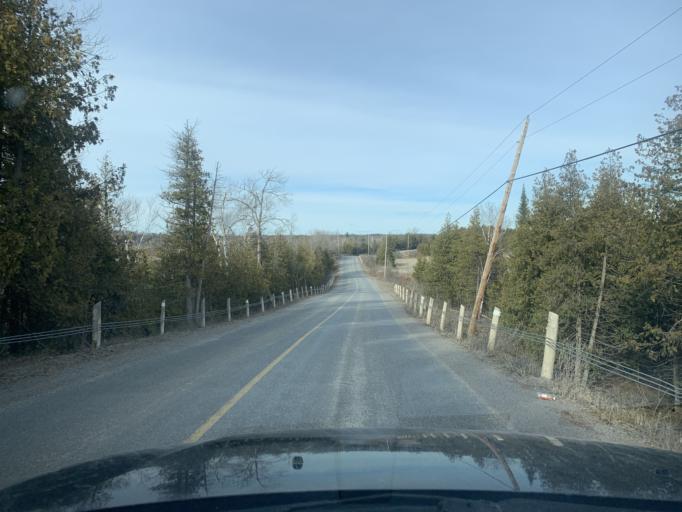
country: CA
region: Ontario
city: Greater Napanee
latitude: 44.4246
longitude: -77.0985
